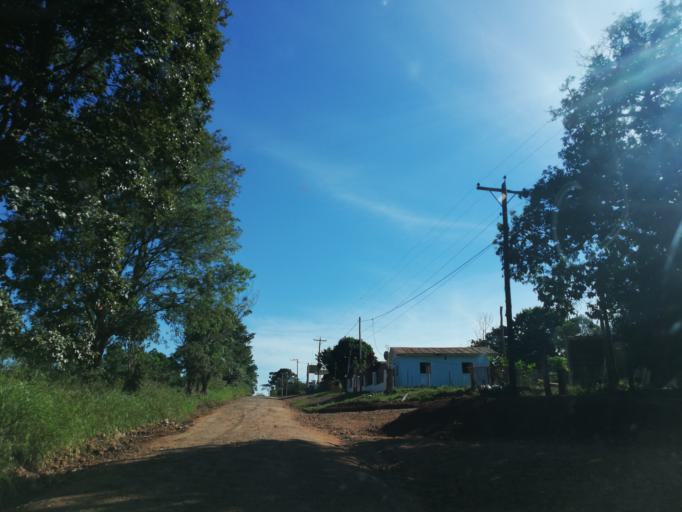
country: AR
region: Misiones
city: Dos de Mayo
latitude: -27.0167
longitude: -54.4554
